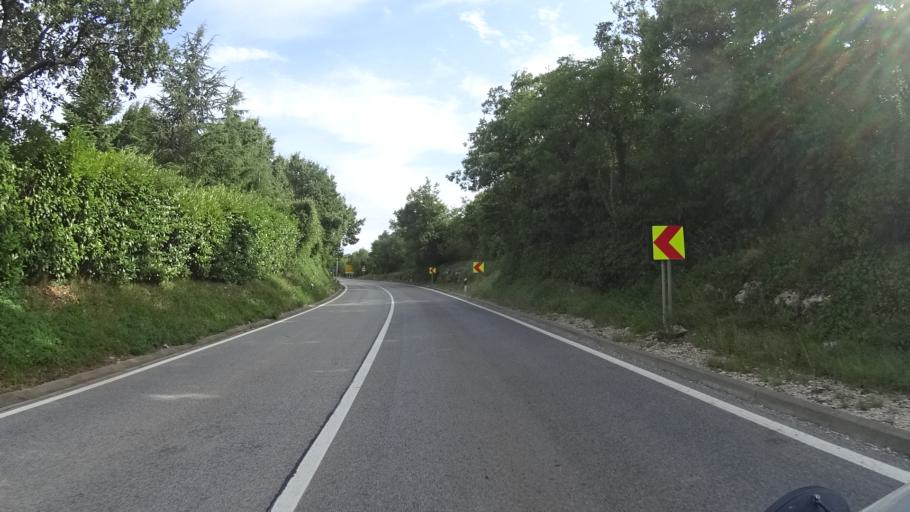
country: HR
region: Istarska
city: Rasa
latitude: 45.0645
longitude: 14.0898
